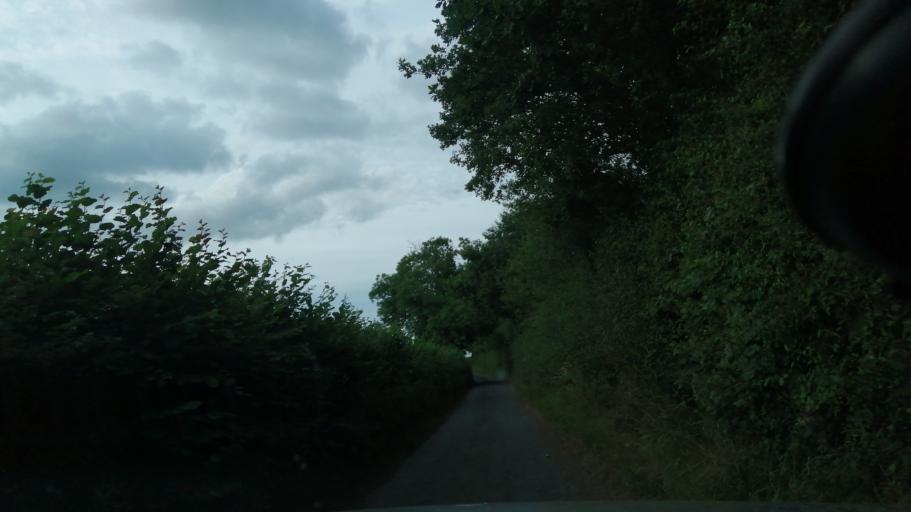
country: GB
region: England
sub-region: Herefordshire
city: Thruxton
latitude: 52.0099
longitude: -2.8030
